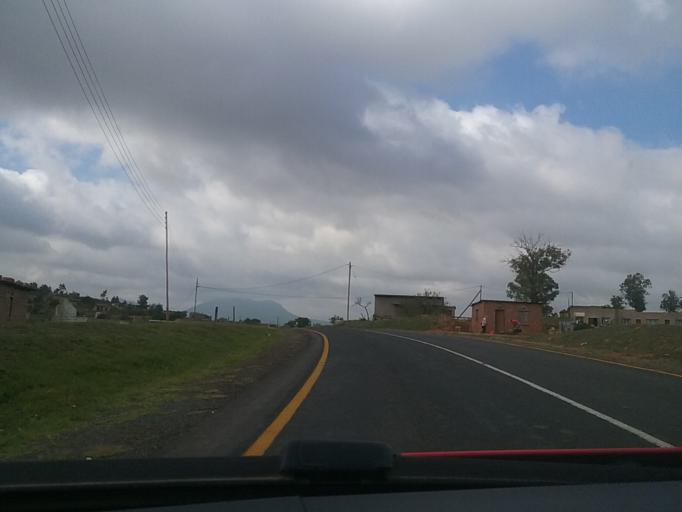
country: LS
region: Berea
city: Teyateyaneng
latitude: -29.1673
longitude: 27.7773
